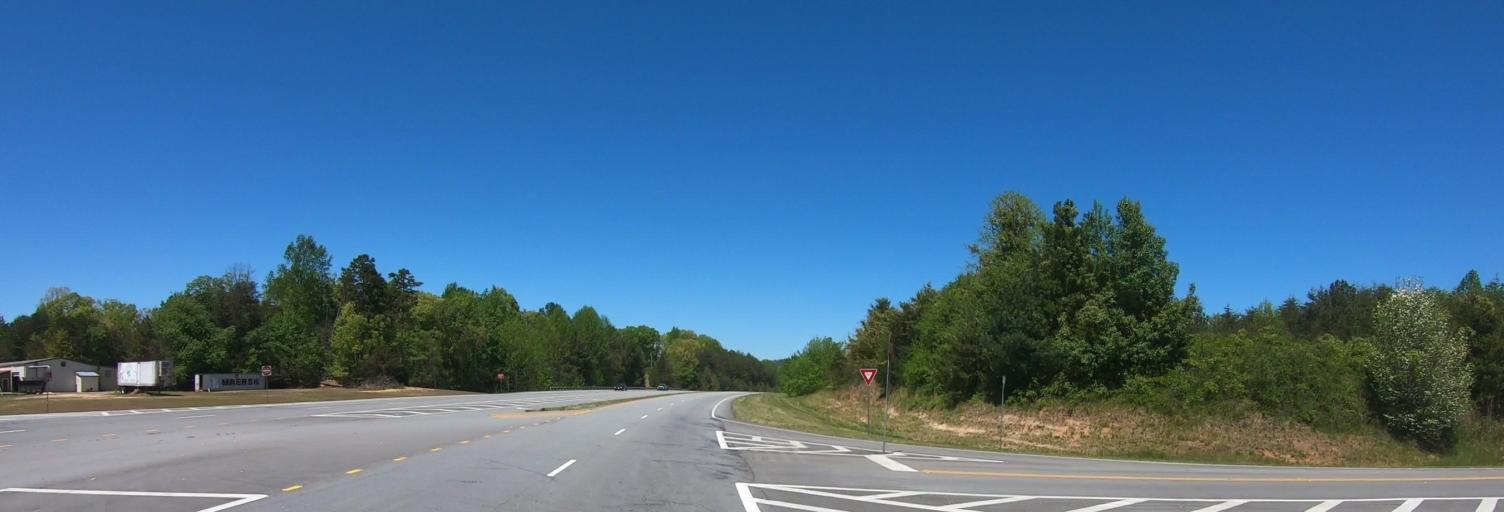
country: US
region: Georgia
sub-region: Habersham County
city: Clarkesville
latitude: 34.6875
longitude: -83.4217
